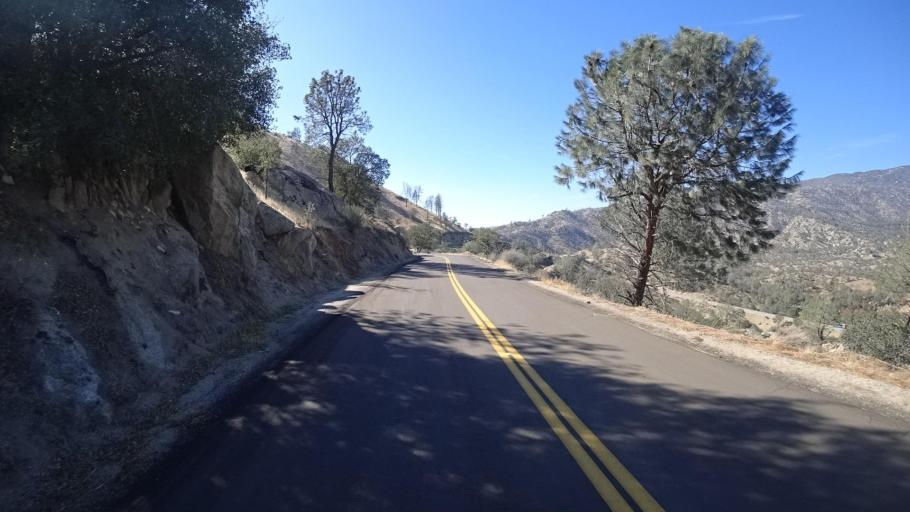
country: US
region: California
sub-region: Kern County
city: Bodfish
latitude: 35.5921
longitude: -118.5171
